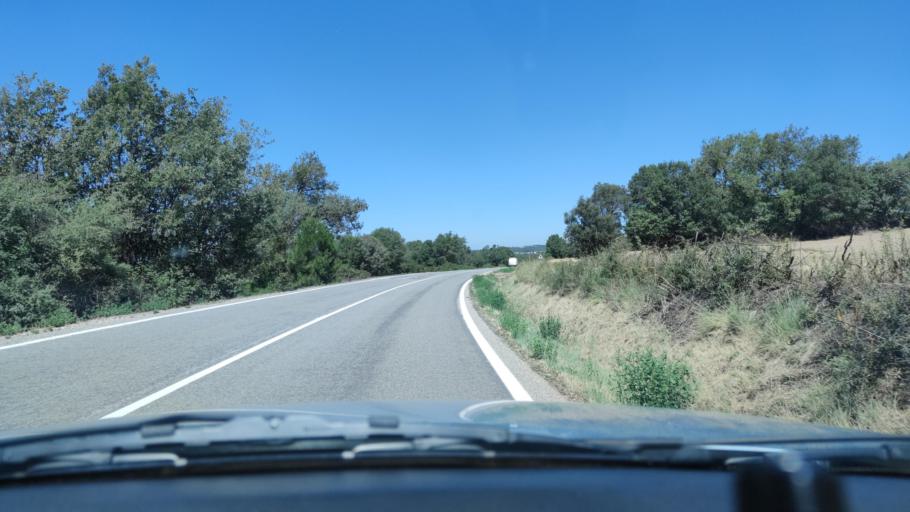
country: ES
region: Catalonia
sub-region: Provincia de Lleida
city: Solsona
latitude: 41.8946
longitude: 1.5498
